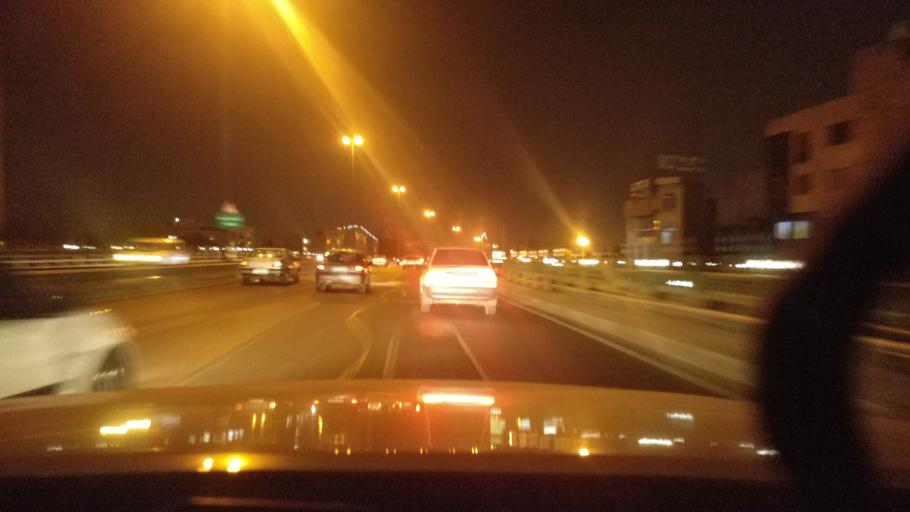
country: IR
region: Tehran
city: Tehran
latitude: 35.7350
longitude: 51.3133
